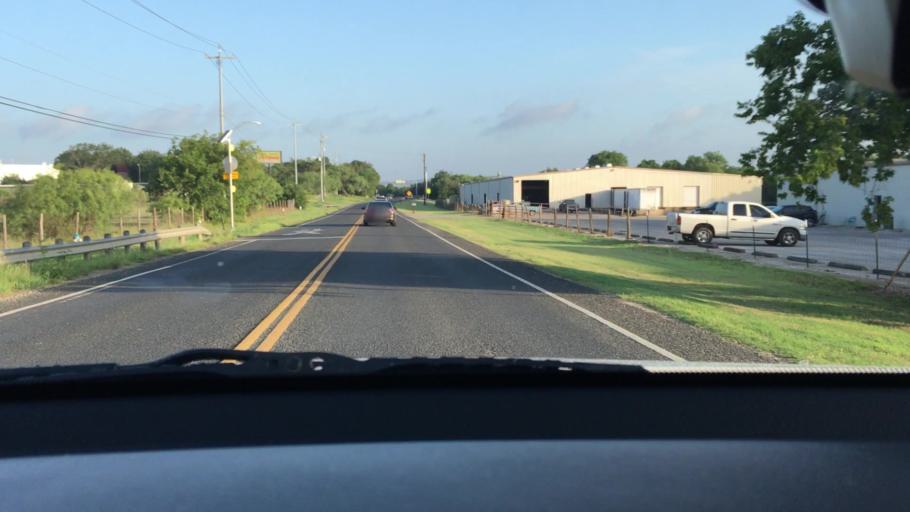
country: US
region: Texas
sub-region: Bexar County
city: Selma
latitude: 29.6081
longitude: -98.3319
